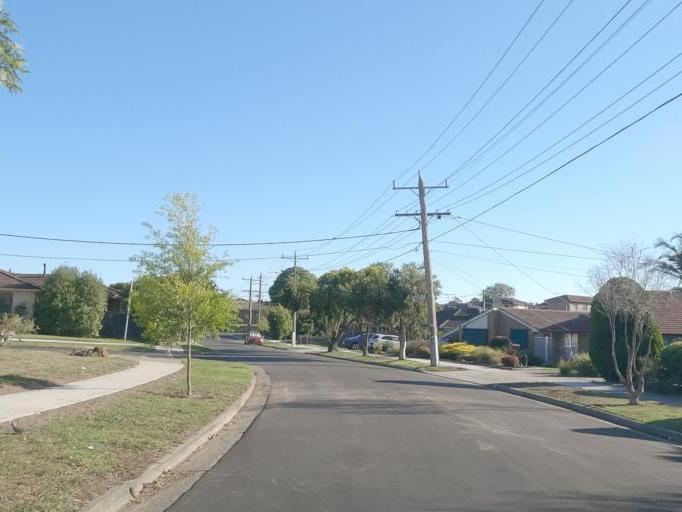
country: AU
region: Victoria
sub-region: Hume
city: Gladstone Park
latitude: -37.6858
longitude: 144.8920
